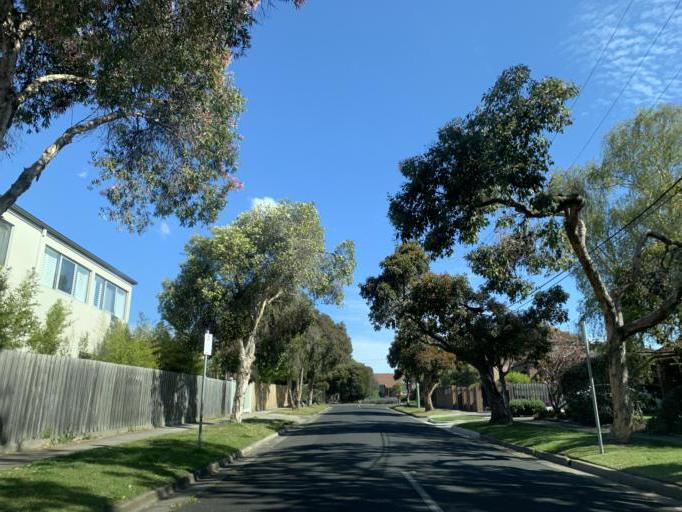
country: AU
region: Victoria
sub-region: Bayside
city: Hampton East
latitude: -37.9423
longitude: 145.0179
